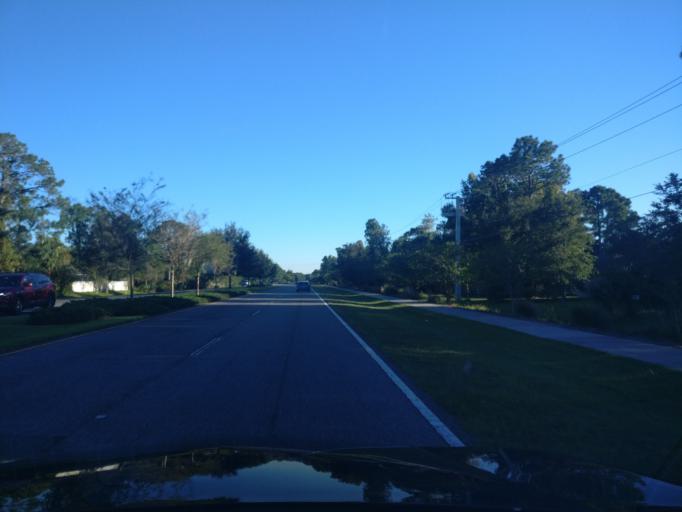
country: US
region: Florida
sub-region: Flagler County
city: Bunnell
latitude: 29.5175
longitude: -81.2241
